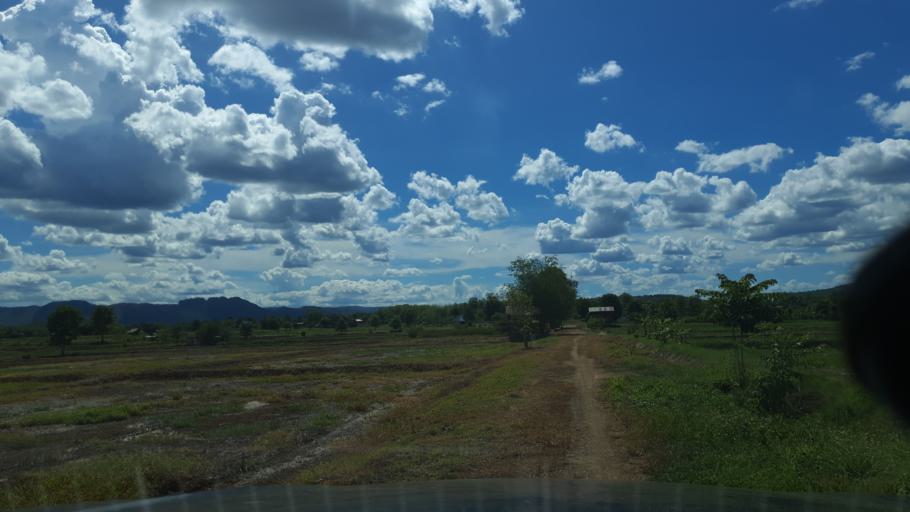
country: TH
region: Sukhothai
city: Thung Saliam
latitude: 17.3379
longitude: 99.4426
